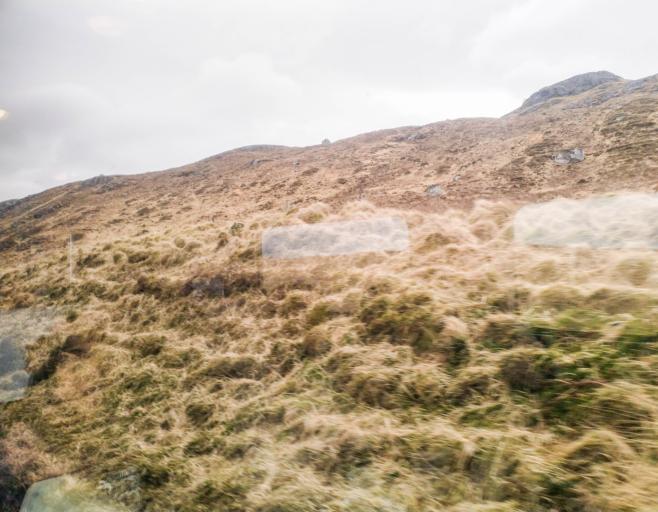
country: GB
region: Scotland
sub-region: Highland
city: Spean Bridge
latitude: 56.5911
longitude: -4.6475
